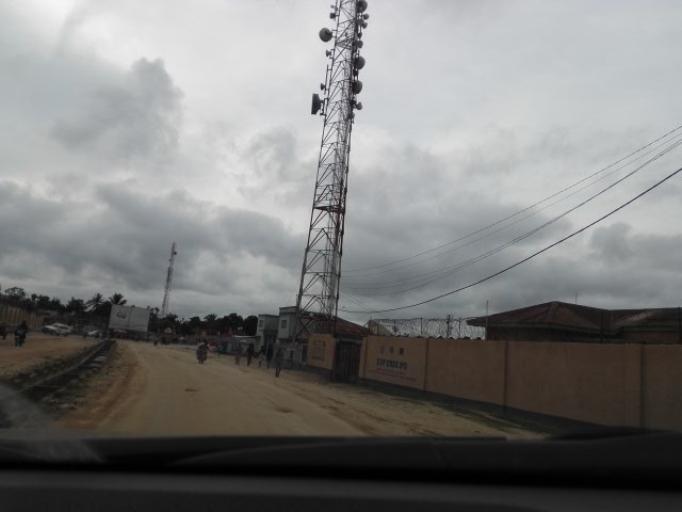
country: CD
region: Eastern Province
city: Bunia
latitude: 1.5517
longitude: 30.2485
